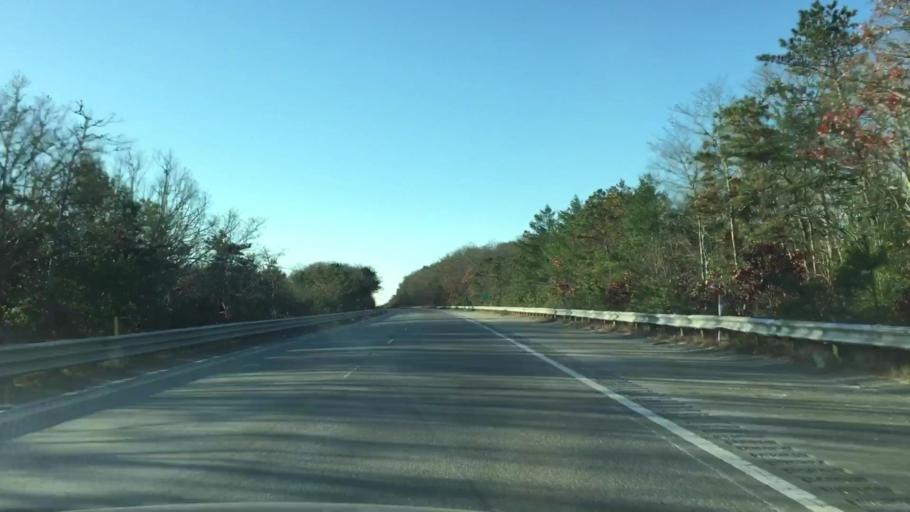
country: US
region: Massachusetts
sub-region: Barnstable County
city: West Falmouth
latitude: 41.6042
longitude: -70.6267
